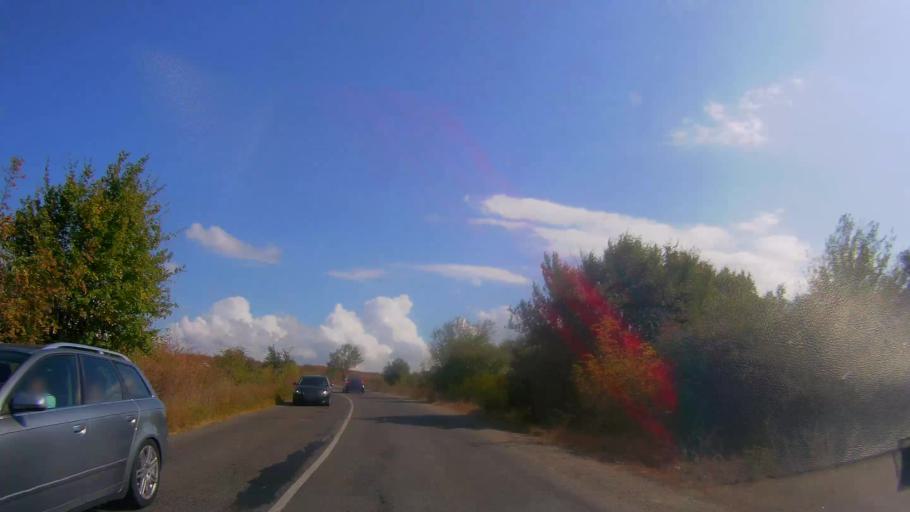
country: BG
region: Burgas
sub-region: Obshtina Burgas
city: Burgas
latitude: 42.4778
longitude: 27.3898
